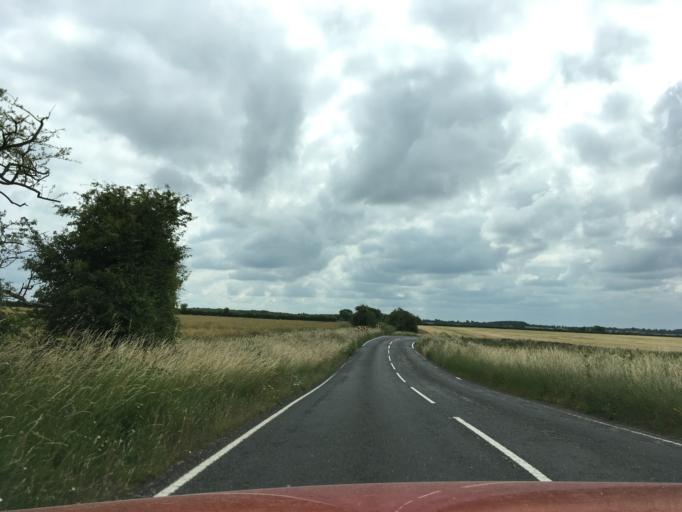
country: GB
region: England
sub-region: Oxfordshire
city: Charlbury
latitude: 51.9102
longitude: -1.4889
